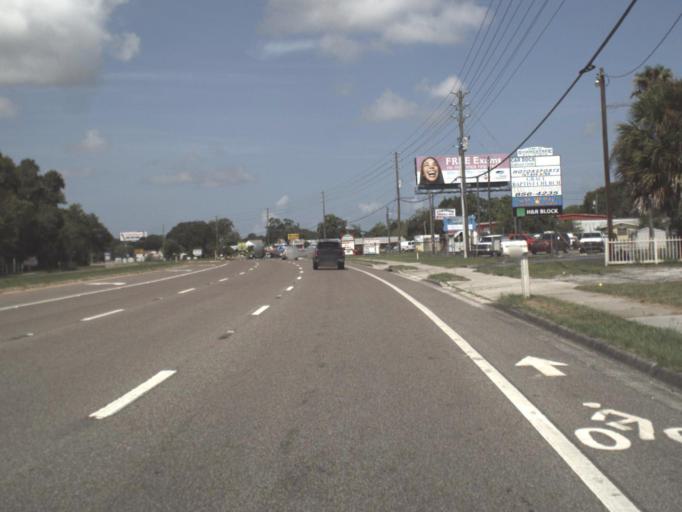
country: US
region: Florida
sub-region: Pasco County
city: Bayonet Point
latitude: 28.3392
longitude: -82.6197
